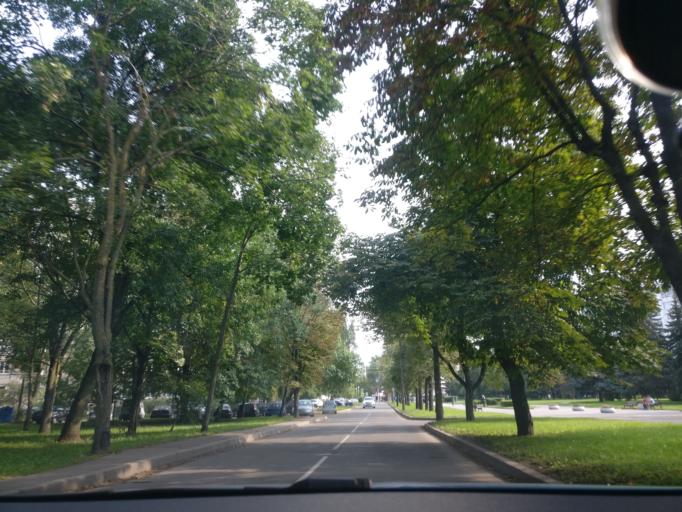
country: BY
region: Minsk
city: Minsk
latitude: 53.9245
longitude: 27.5756
